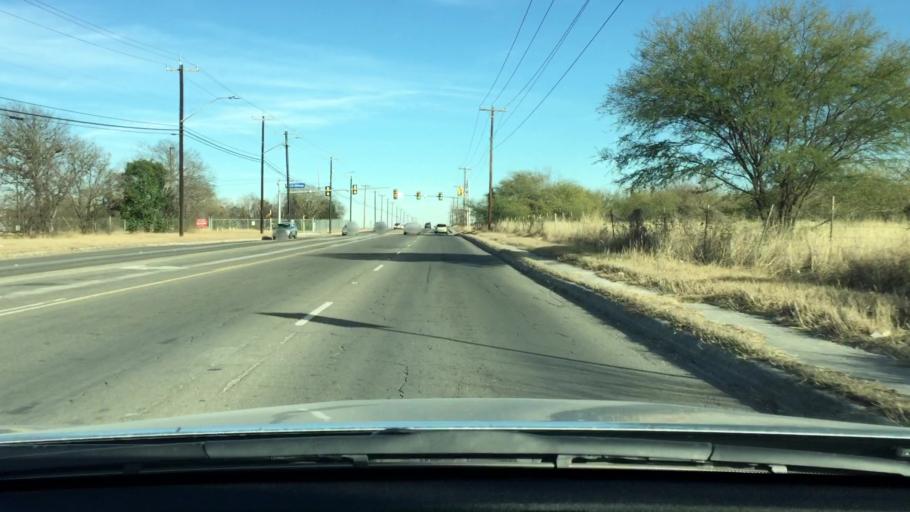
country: US
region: Texas
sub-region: Bexar County
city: Kirby
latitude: 29.4841
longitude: -98.3785
